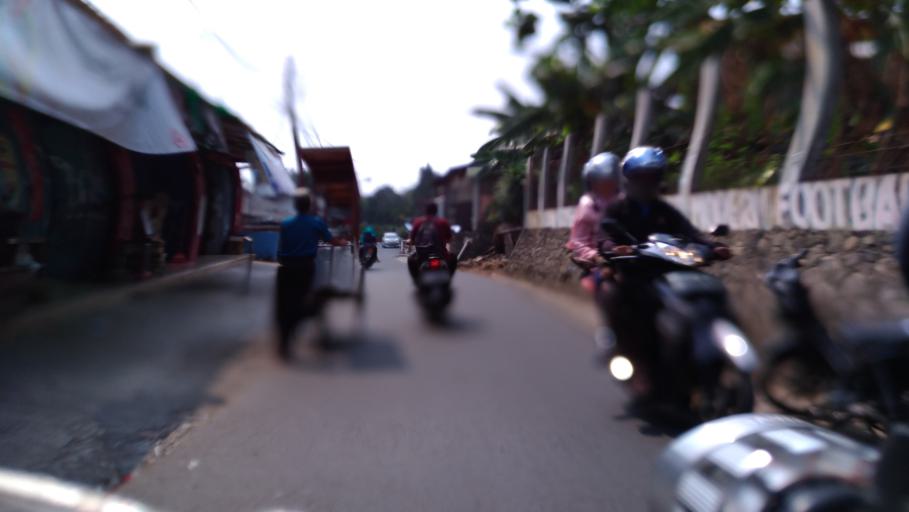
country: ID
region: West Java
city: Depok
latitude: -6.3563
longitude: 106.8745
